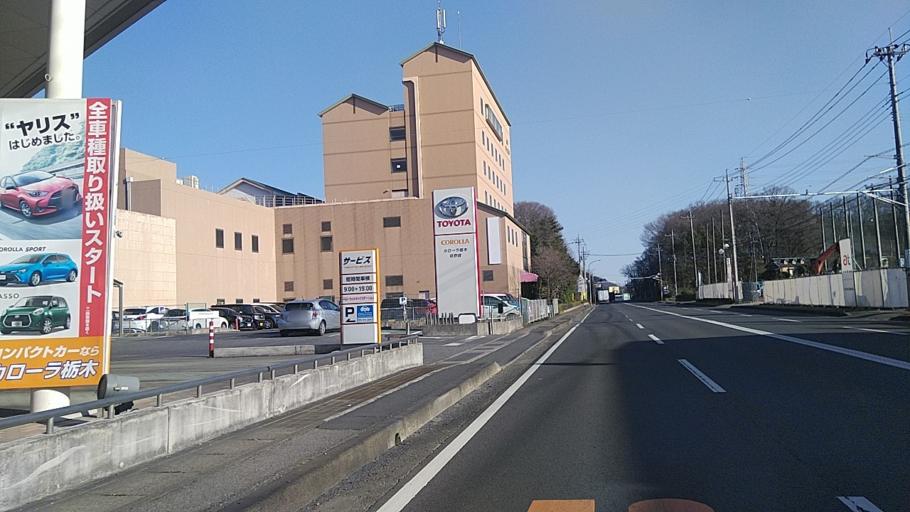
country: JP
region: Tochigi
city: Sano
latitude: 36.3325
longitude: 139.5837
